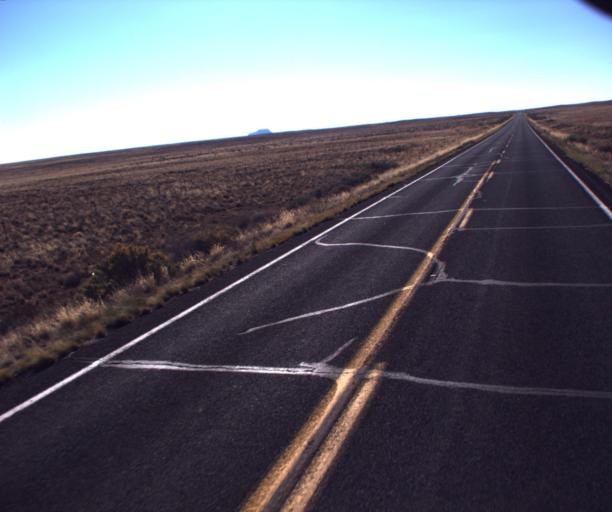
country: US
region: Arizona
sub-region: Navajo County
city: First Mesa
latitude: 35.6599
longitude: -110.4927
